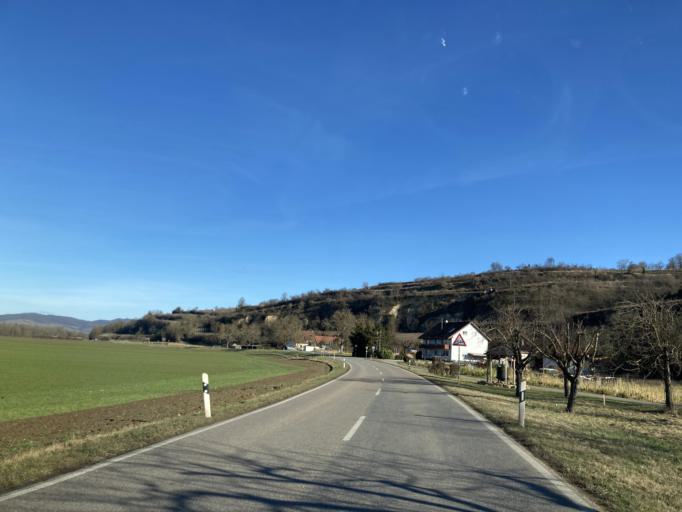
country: DE
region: Baden-Wuerttemberg
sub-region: Freiburg Region
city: Merdingen
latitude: 47.9902
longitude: 7.6705
